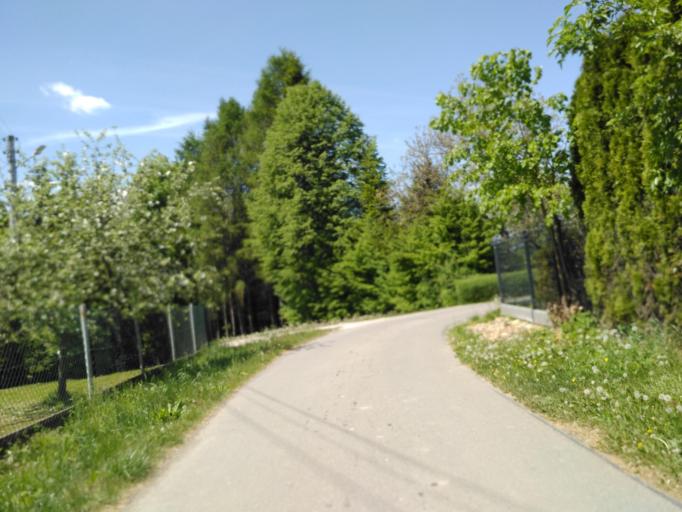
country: PL
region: Subcarpathian Voivodeship
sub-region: Powiat krosnienski
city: Chorkowka
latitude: 49.6791
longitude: 21.6955
